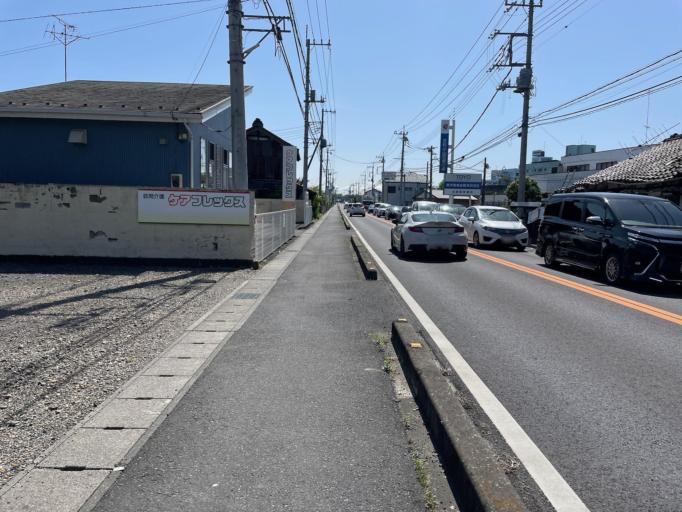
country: JP
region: Tochigi
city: Sano
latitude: 36.3154
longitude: 139.5294
